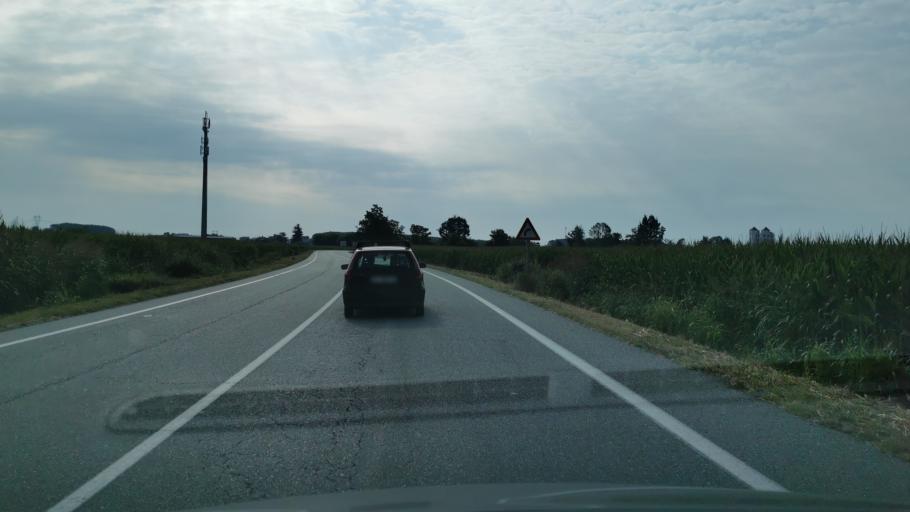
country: IT
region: Piedmont
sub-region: Provincia di Torino
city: Cercenasco
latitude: 44.8641
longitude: 7.5025
